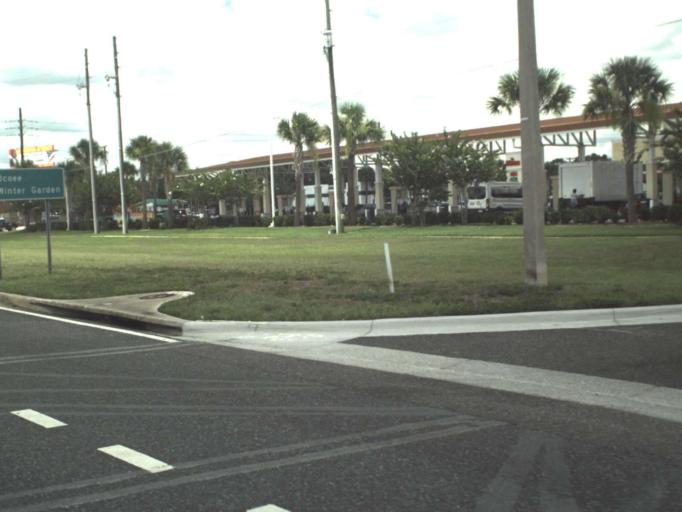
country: US
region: Florida
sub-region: Orange County
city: Fairview Shores
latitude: 28.5770
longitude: -81.4163
